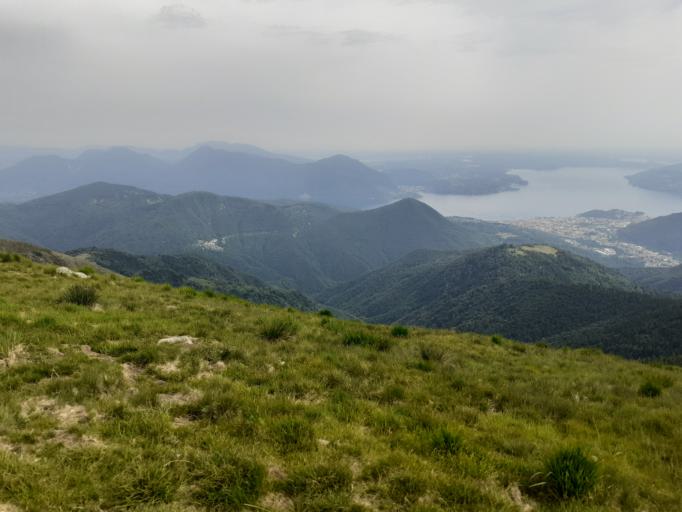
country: IT
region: Piedmont
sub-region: Provincia Verbano-Cusio-Ossola
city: Intragna
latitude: 46.0161
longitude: 8.5403
